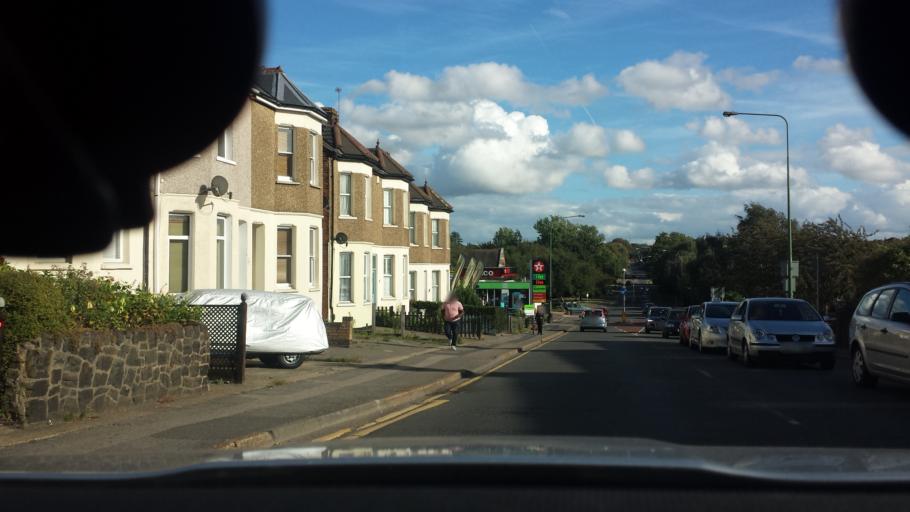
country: GB
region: England
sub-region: Kent
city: Swanley
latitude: 51.3947
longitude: 0.1792
